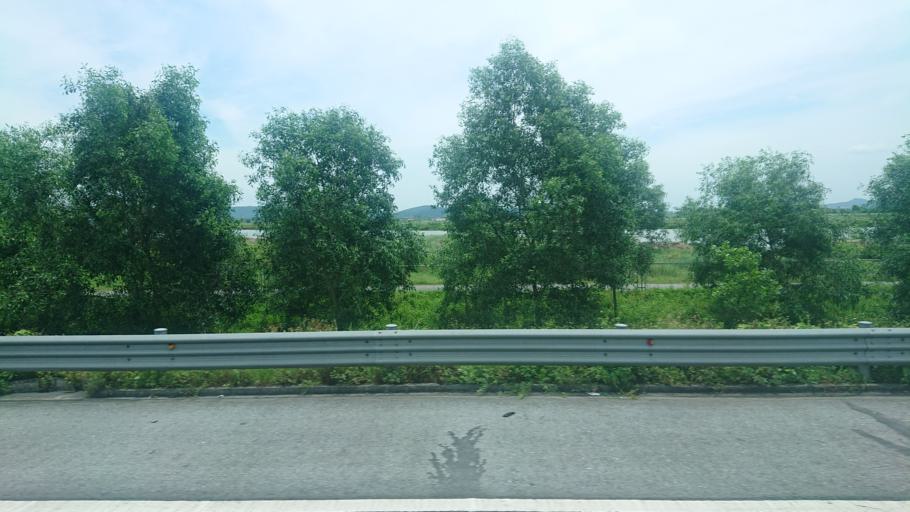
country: VN
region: Hai Phong
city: An Lao
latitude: 20.7810
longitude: 106.5688
